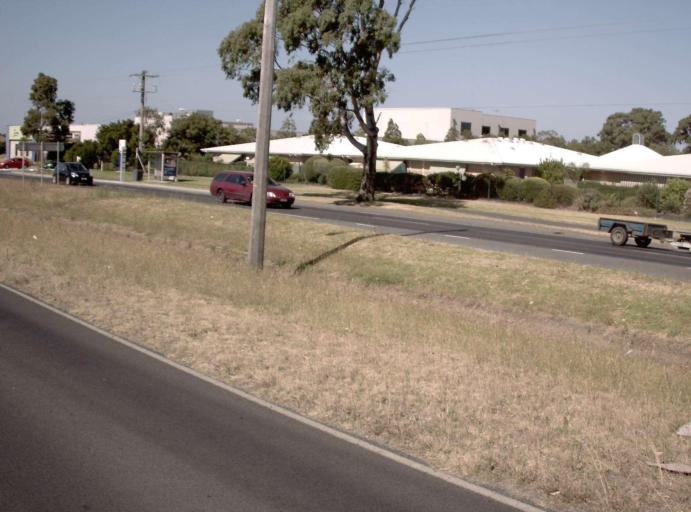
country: AU
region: Victoria
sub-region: Frankston
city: Carrum Downs
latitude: -38.0893
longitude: 145.1806
